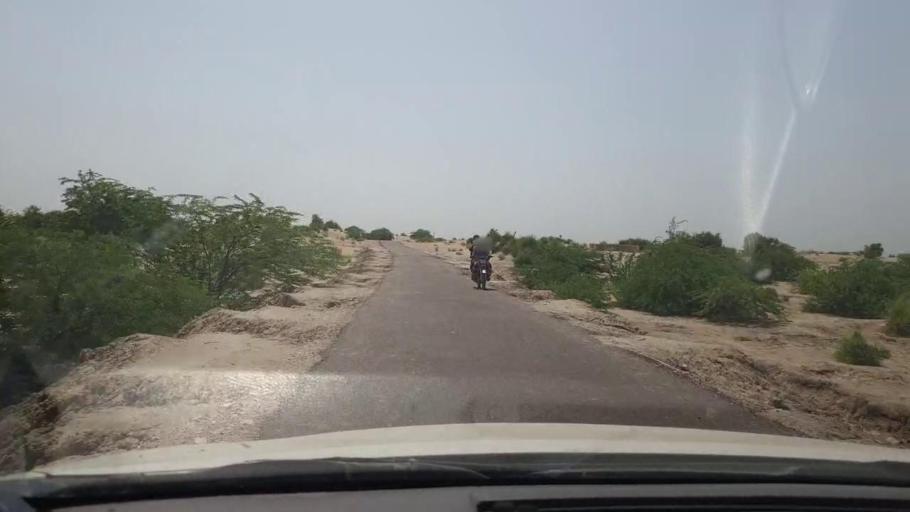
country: PK
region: Sindh
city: Rohri
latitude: 27.5205
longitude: 69.0692
